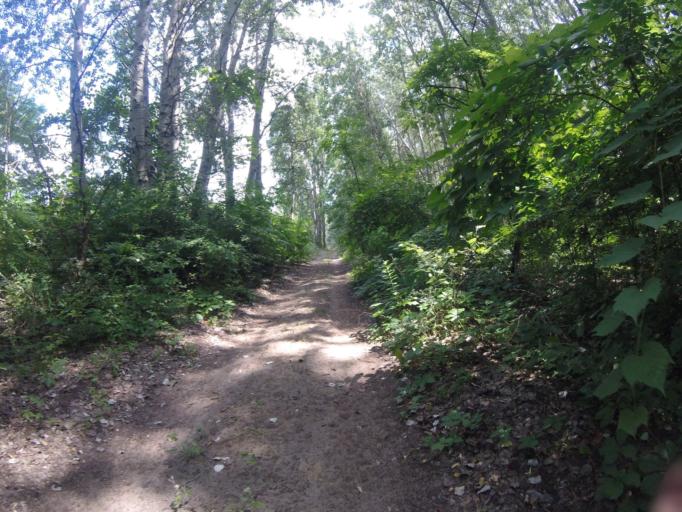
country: HU
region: Bacs-Kiskun
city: Jaszszentlaszlo
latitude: 46.6032
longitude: 19.7155
